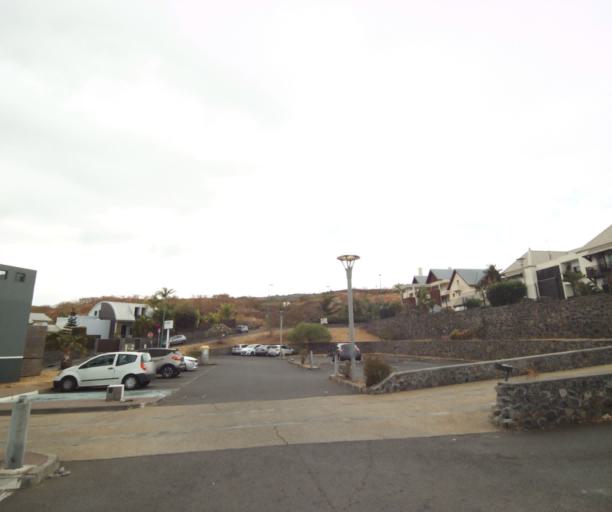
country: RE
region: Reunion
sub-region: Reunion
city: Saint-Paul
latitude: -21.0602
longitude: 55.2297
